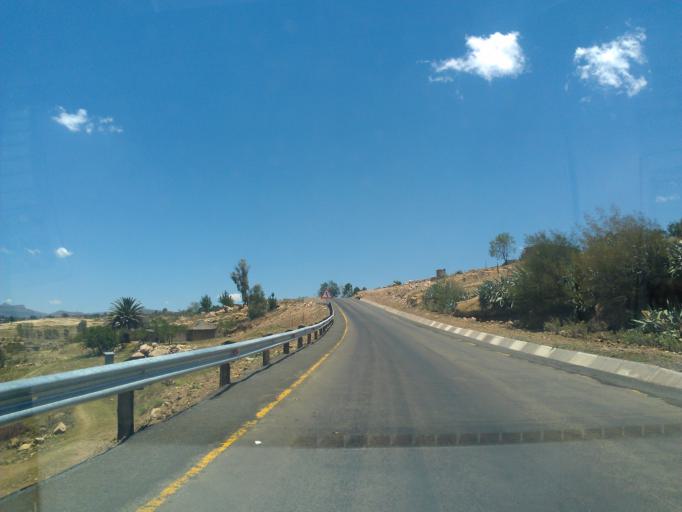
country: LS
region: Leribe
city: Maputsoe
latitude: -29.0935
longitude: 27.9624
